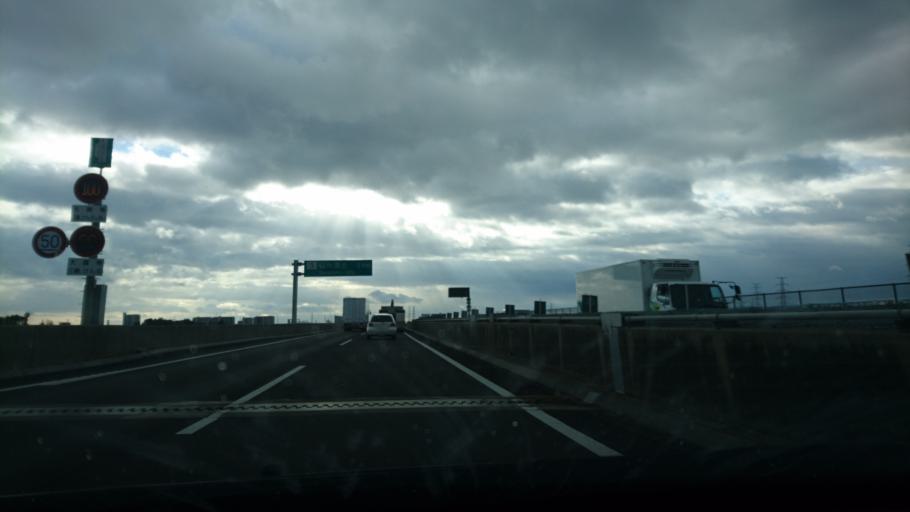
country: JP
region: Miyagi
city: Rifu
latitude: 38.2989
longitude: 140.9852
